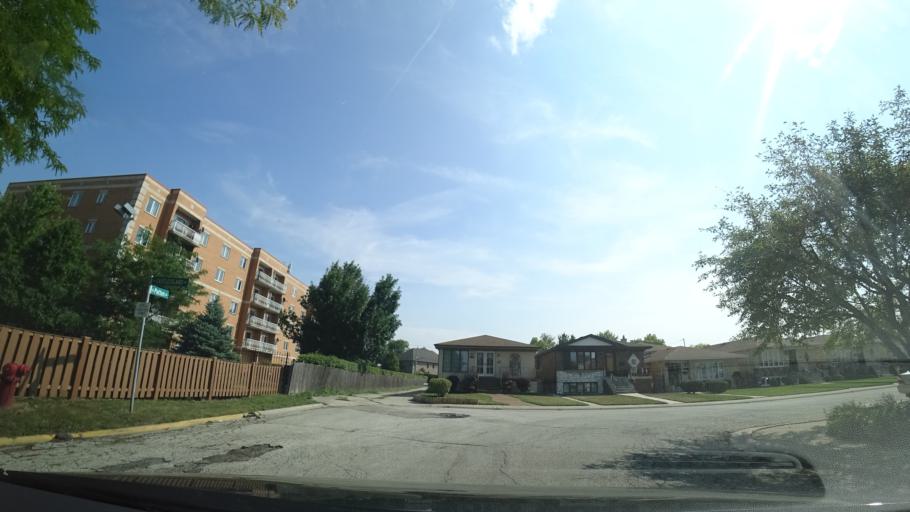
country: US
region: Illinois
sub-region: Cook County
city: Norridge
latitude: 41.9624
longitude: -87.8375
